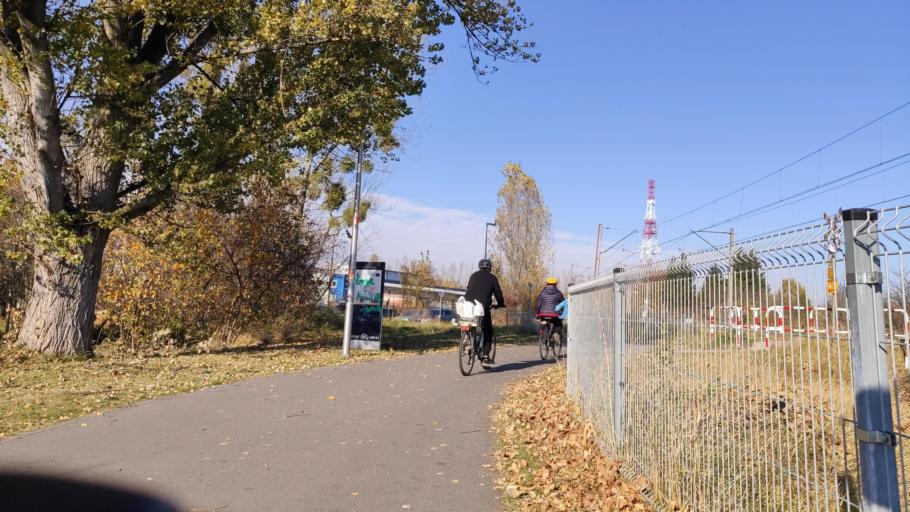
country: PL
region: Lower Silesian Voivodeship
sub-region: Powiat wroclawski
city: Zerniki Wroclawskie
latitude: 51.0677
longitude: 17.0640
